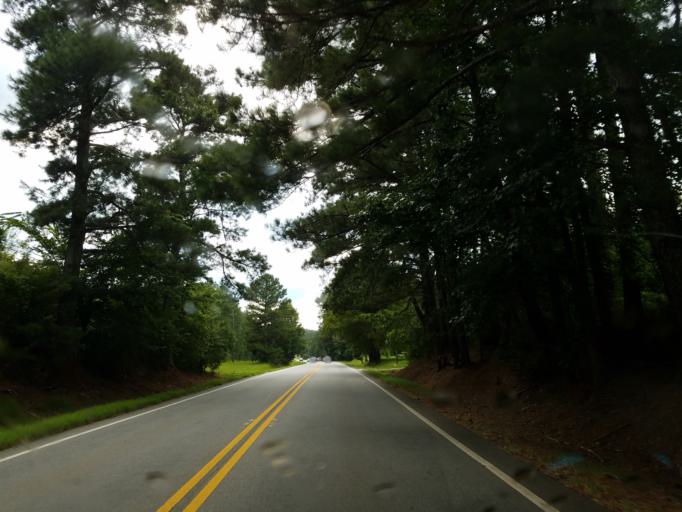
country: US
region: Georgia
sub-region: Floyd County
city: Shannon
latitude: 34.3685
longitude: -85.0823
